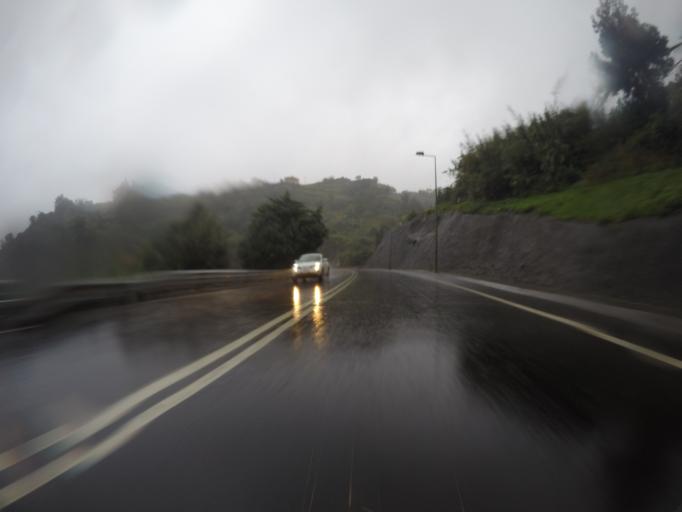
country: PT
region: Madeira
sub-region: Santana
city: Santana
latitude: 32.7572
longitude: -16.8297
